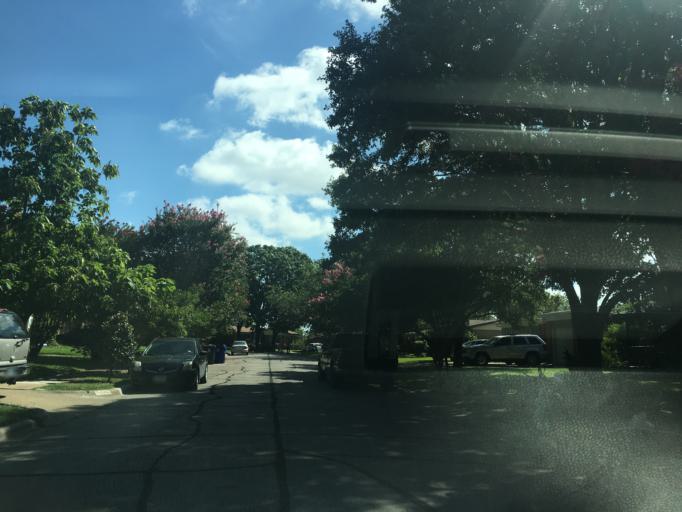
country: US
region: Texas
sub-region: Dallas County
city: Garland
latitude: 32.8422
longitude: -96.6593
